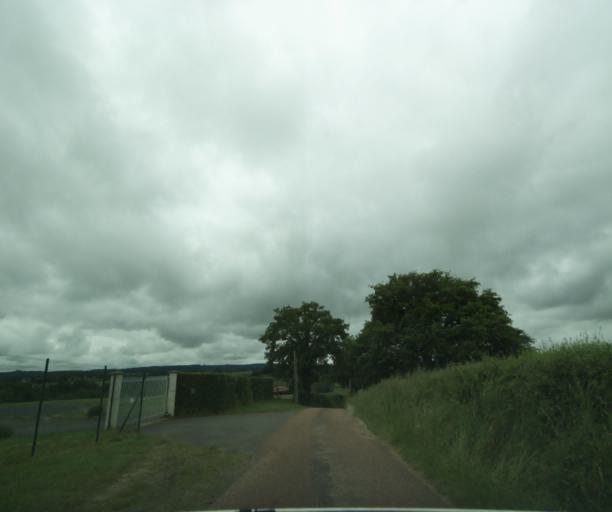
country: FR
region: Bourgogne
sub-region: Departement de Saone-et-Loire
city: Charolles
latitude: 46.4744
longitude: 4.3504
